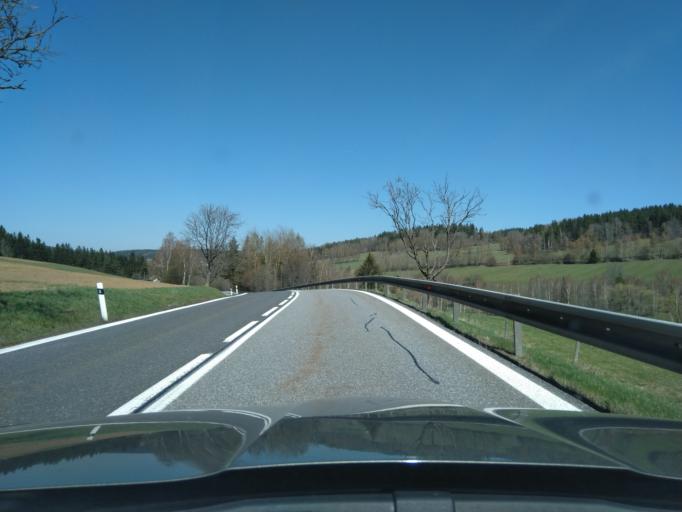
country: CZ
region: Jihocesky
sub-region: Okres Prachatice
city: Vimperk
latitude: 49.0209
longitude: 13.7684
